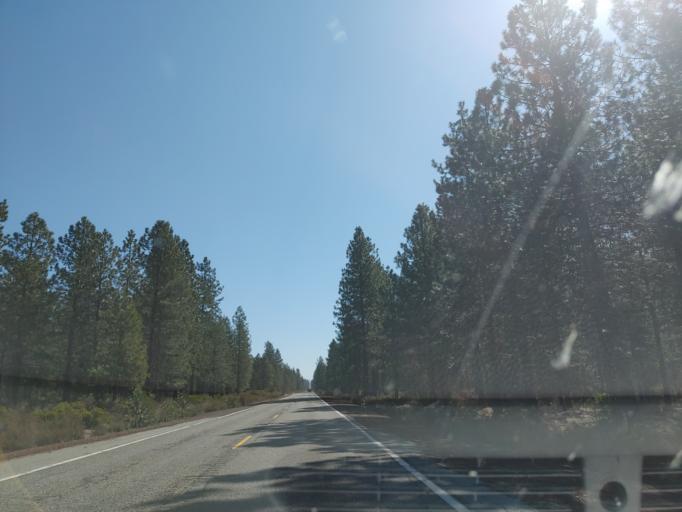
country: US
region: California
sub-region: Siskiyou County
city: McCloud
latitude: 41.2529
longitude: -122.0969
